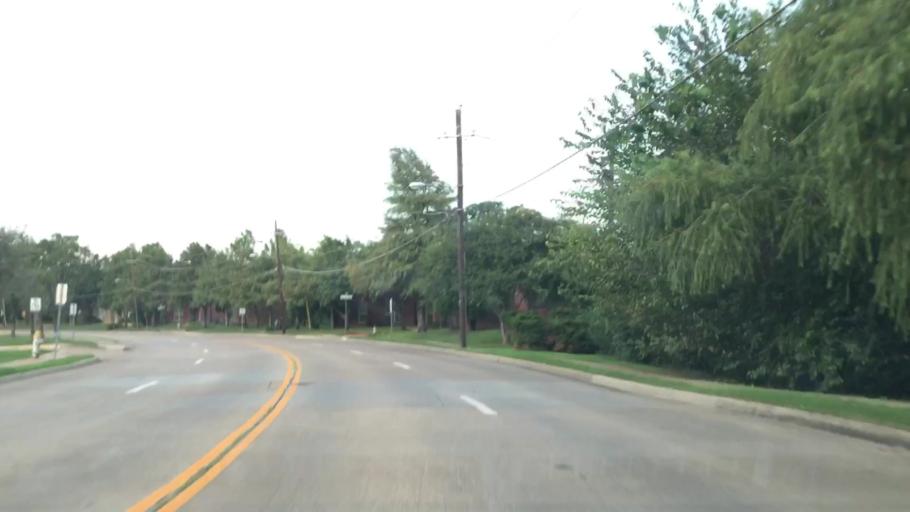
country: US
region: Texas
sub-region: Dallas County
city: Addison
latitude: 32.9987
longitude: -96.8649
